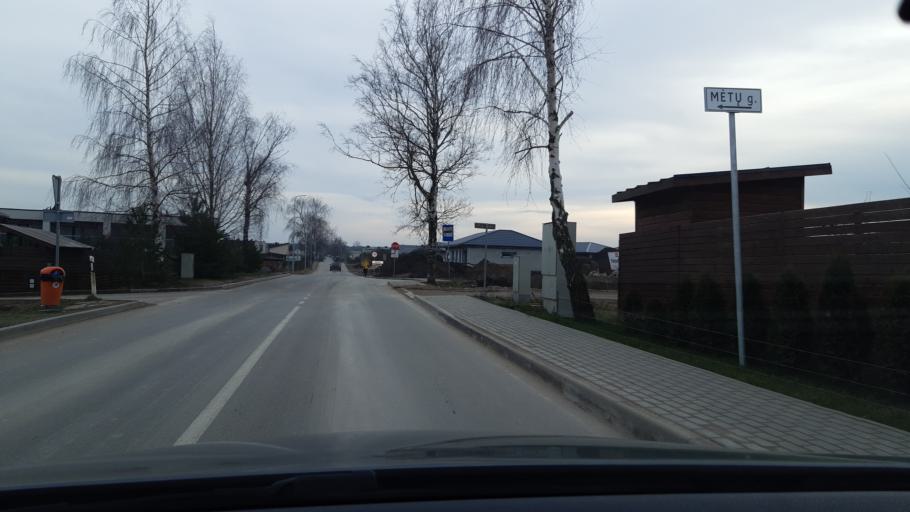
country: LT
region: Kauno apskritis
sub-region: Kauno rajonas
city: Akademija (Kaunas)
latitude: 54.9483
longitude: 23.8285
